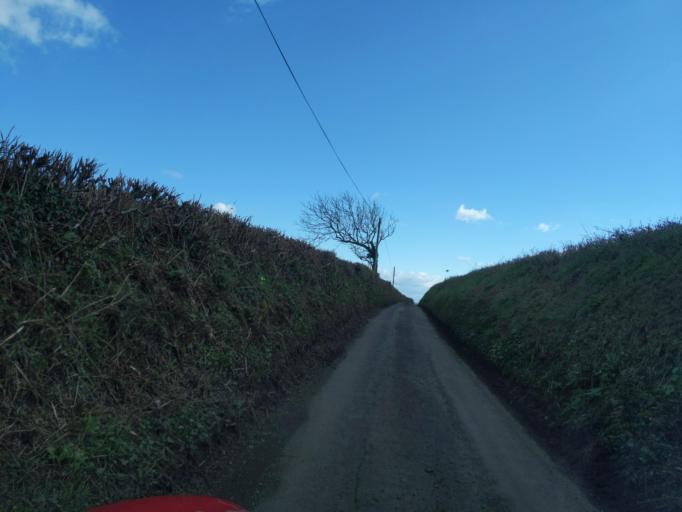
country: GB
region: England
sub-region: Devon
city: Kingsbridge
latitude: 50.2979
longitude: -3.7910
